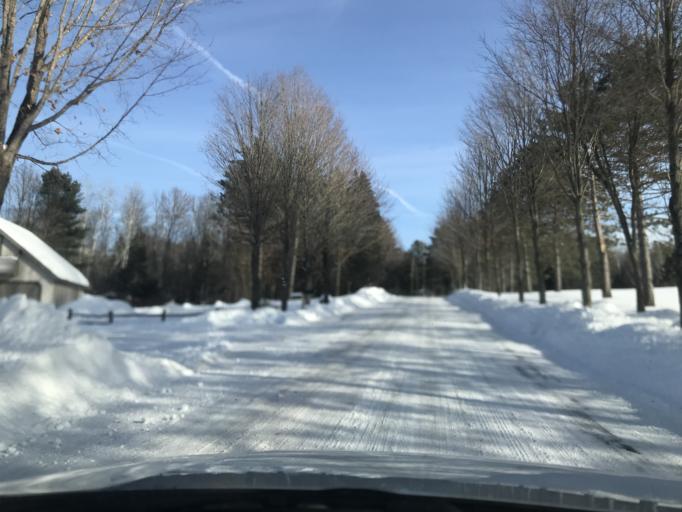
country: US
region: Wisconsin
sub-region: Menominee County
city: Legend Lake
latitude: 45.2980
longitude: -88.4938
